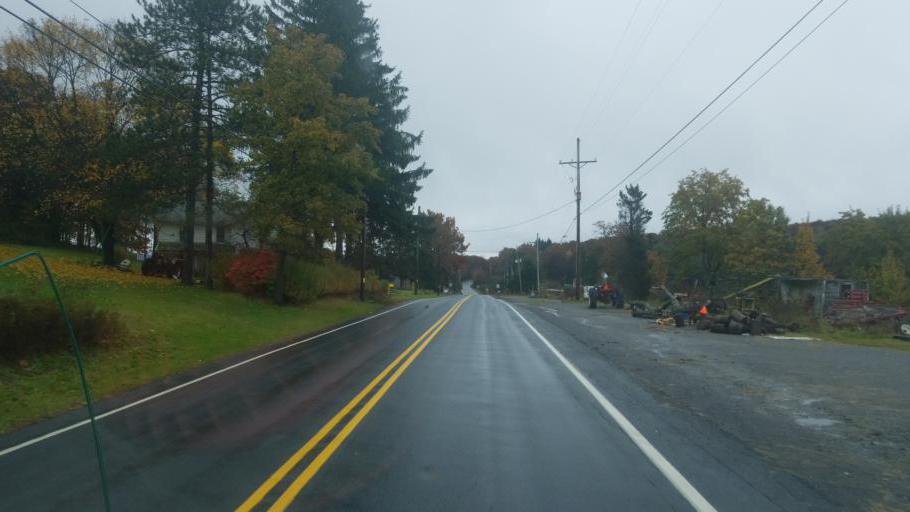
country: US
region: Pennsylvania
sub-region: Centre County
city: Milesburg
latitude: 41.0289
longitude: -77.9663
